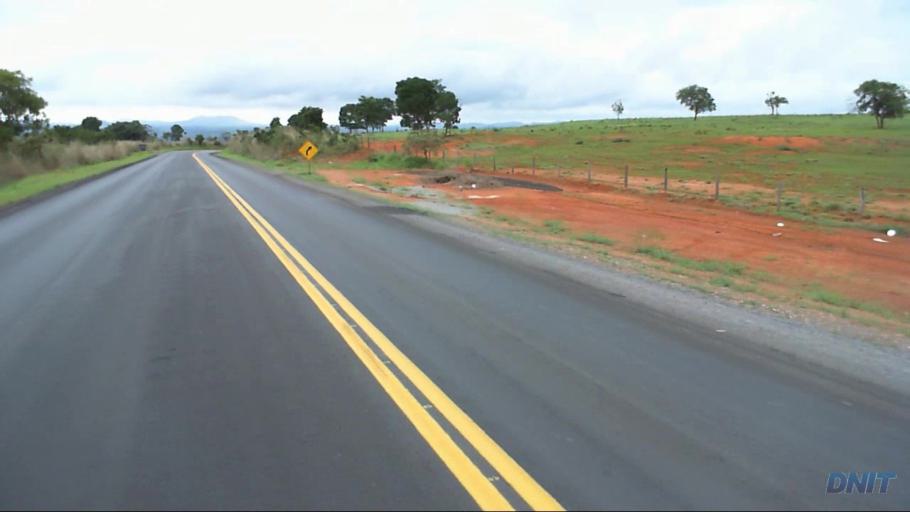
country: BR
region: Goias
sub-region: Padre Bernardo
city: Padre Bernardo
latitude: -15.2209
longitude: -48.5224
